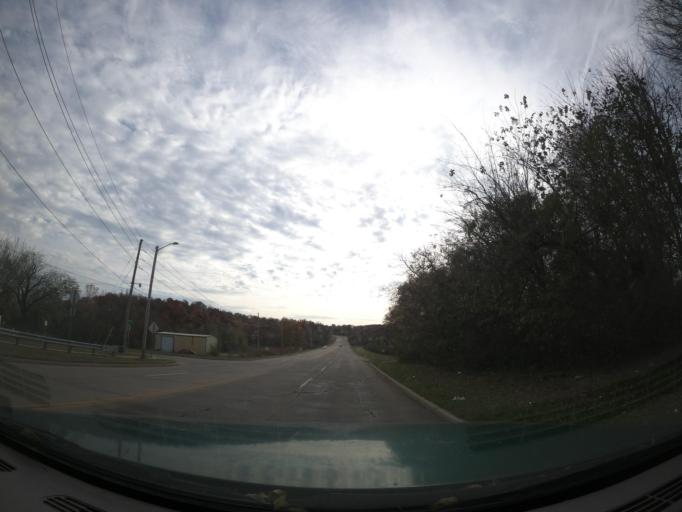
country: US
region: Oklahoma
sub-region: Tulsa County
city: Turley
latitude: 36.2178
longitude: -95.9937
